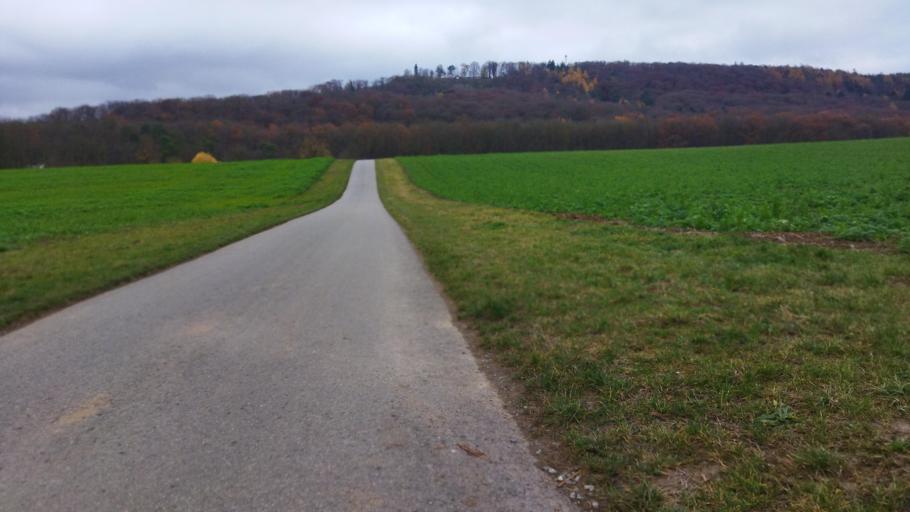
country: DE
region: Baden-Wuerttemberg
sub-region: Regierungsbezirk Stuttgart
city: Leingarten
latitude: 49.1366
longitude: 9.1055
